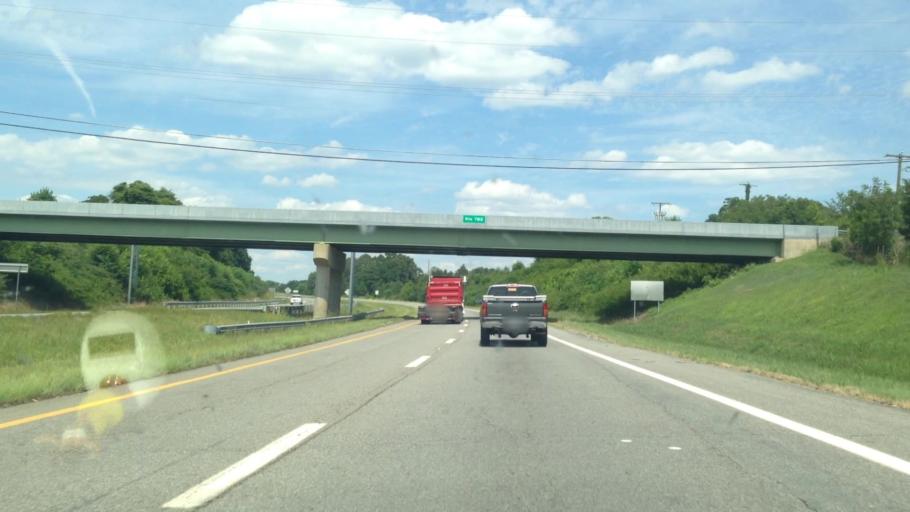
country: US
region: Virginia
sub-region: Henry County
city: Chatmoss
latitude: 36.6234
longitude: -79.8527
